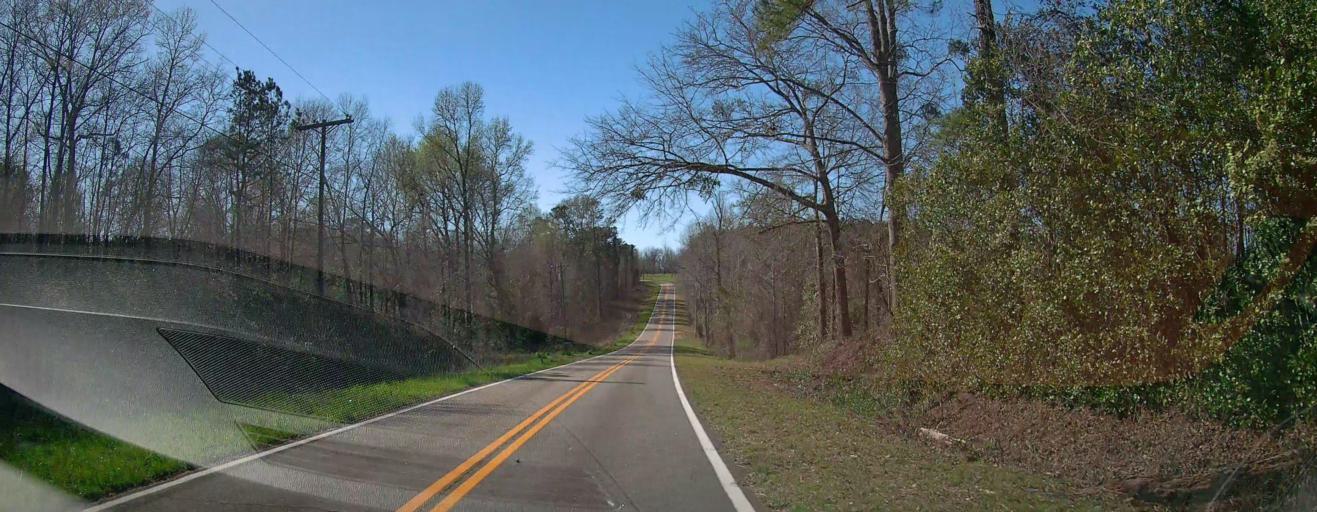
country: US
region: Georgia
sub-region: Peach County
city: Fort Valley
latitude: 32.6115
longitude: -83.8976
